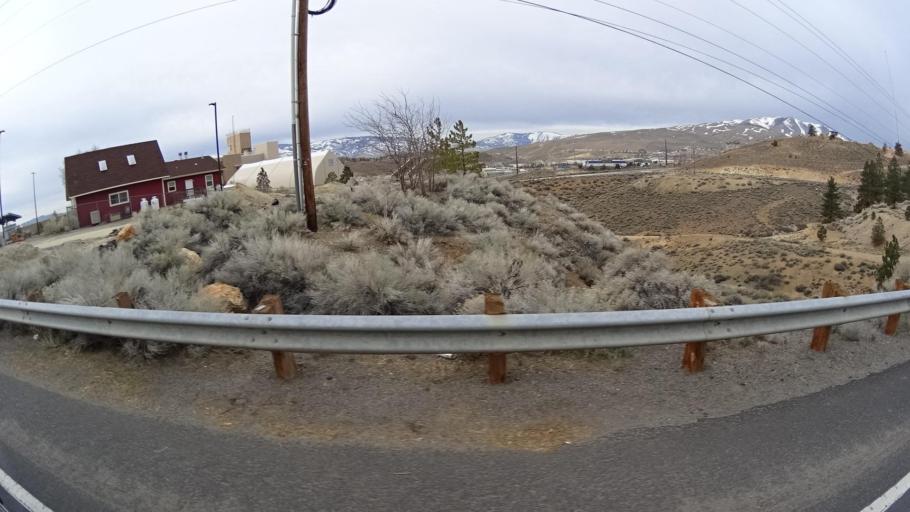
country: US
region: Nevada
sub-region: Washoe County
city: Sun Valley
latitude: 39.5736
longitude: -119.8013
